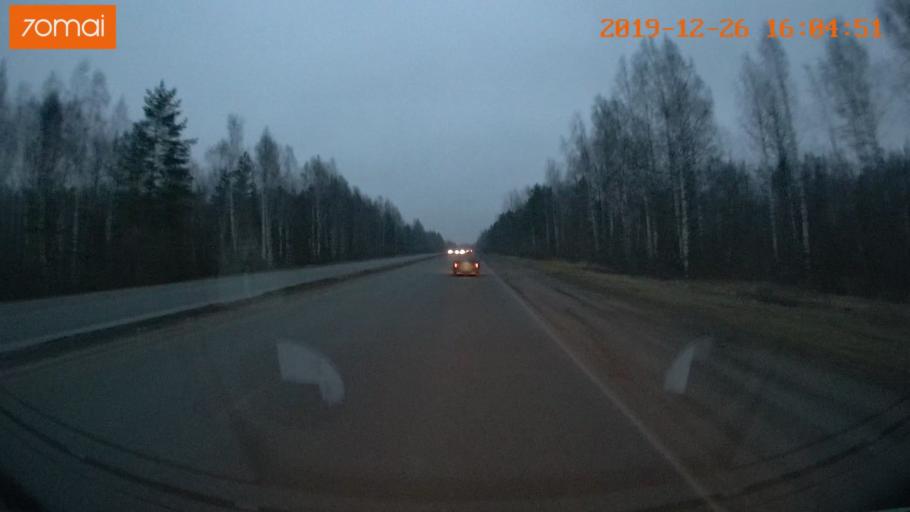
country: RU
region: Jaroslavl
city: Rybinsk
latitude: 58.0082
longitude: 38.8806
